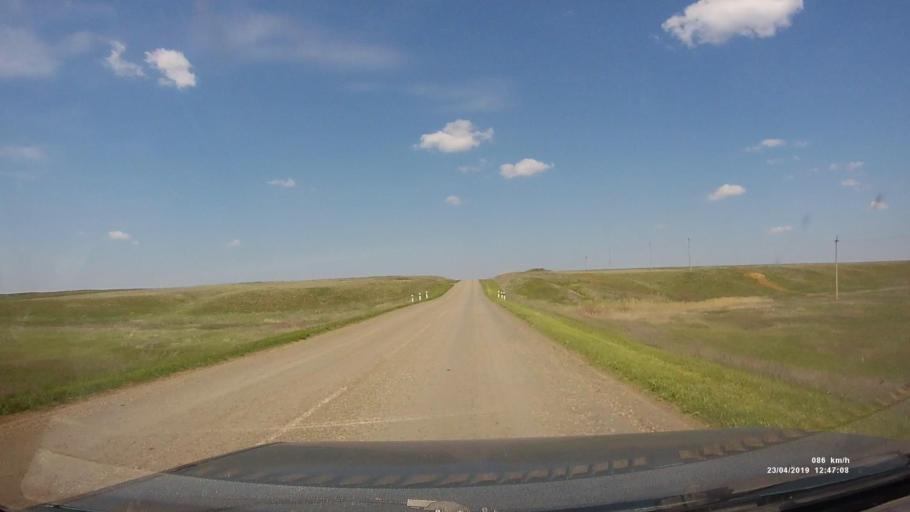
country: RU
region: Kalmykiya
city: Yashalta
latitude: 46.5084
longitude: 42.6385
